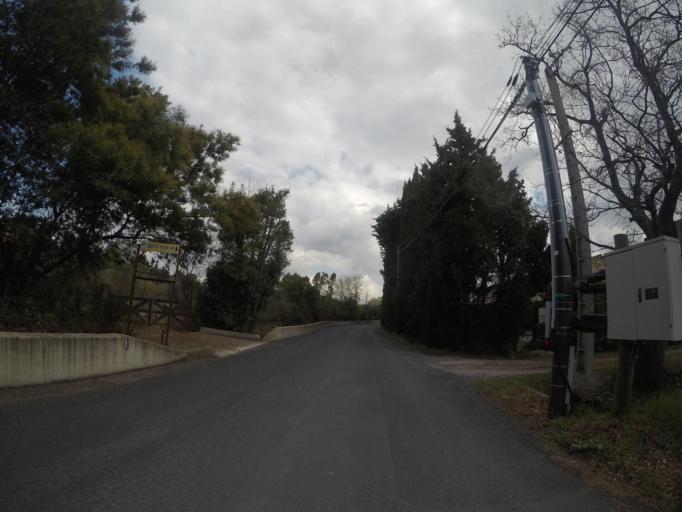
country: FR
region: Languedoc-Roussillon
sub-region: Departement des Pyrenees-Orientales
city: Le Soler
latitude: 42.6753
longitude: 2.7812
